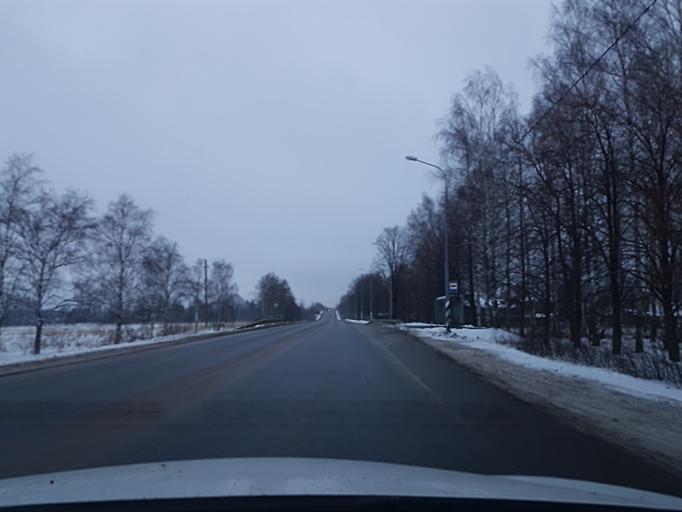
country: RU
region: Tverskaya
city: Novozavidovskiy
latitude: 56.5587
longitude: 36.4132
